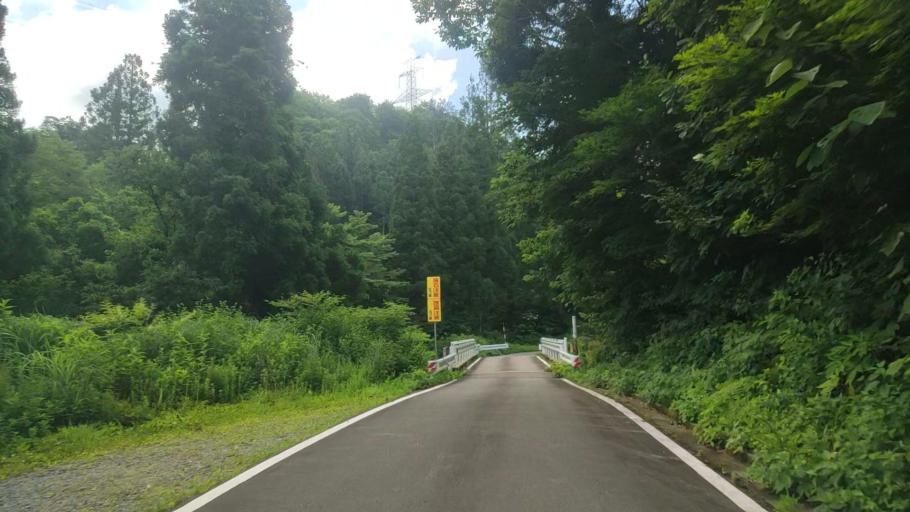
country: JP
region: Fukui
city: Katsuyama
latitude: 36.1722
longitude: 136.5241
